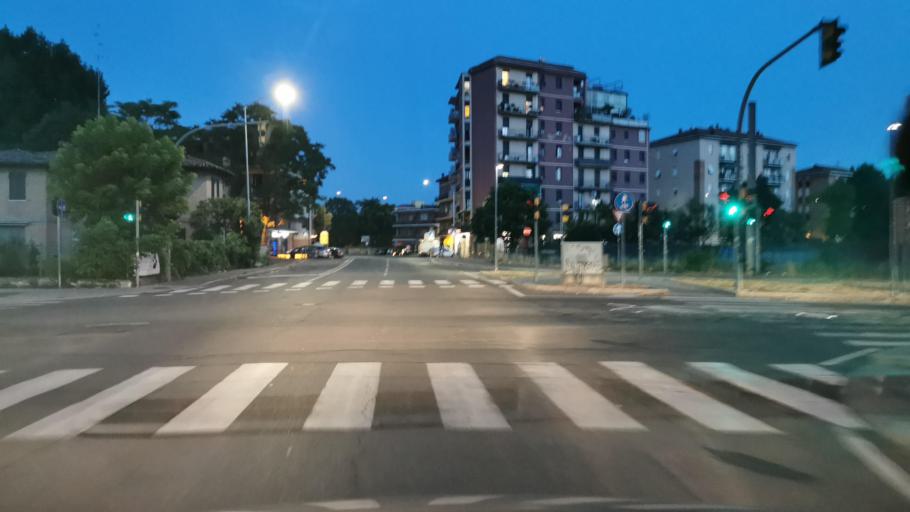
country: IT
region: Emilia-Romagna
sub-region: Provincia di Modena
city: Modena
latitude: 44.6361
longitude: 10.9341
